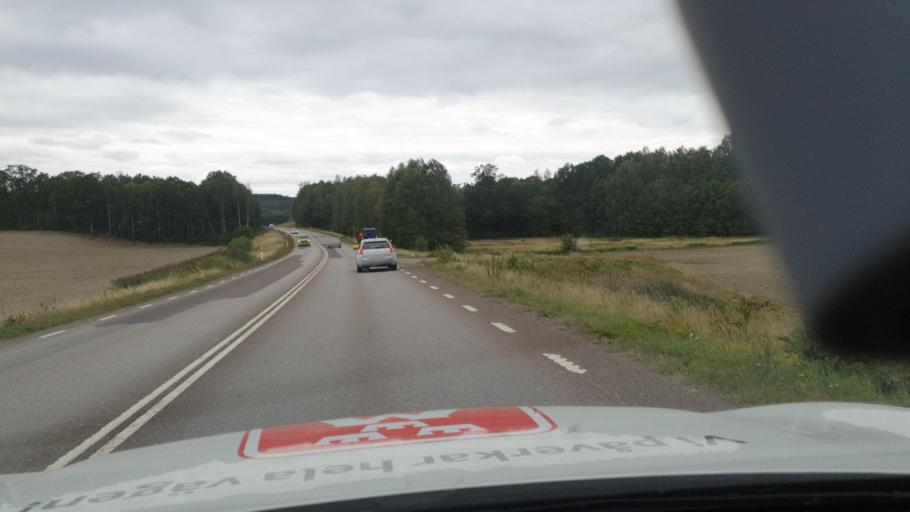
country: SE
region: Vaestra Goetaland
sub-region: Melleruds Kommun
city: Mellerud
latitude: 58.7274
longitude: 12.3808
